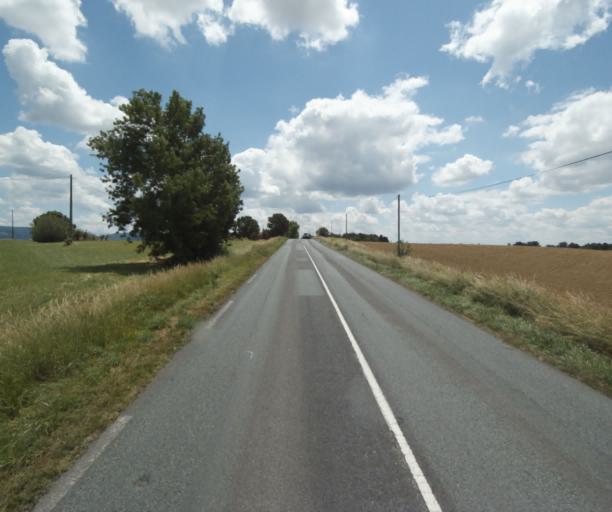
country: FR
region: Midi-Pyrenees
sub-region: Departement de la Haute-Garonne
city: Revel
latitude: 43.5033
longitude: 2.0116
